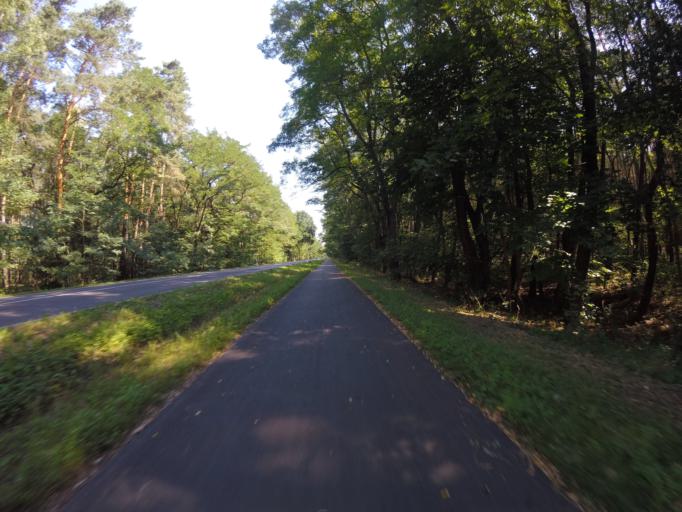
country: DE
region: Brandenburg
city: Mullrose
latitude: 52.2609
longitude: 14.4297
